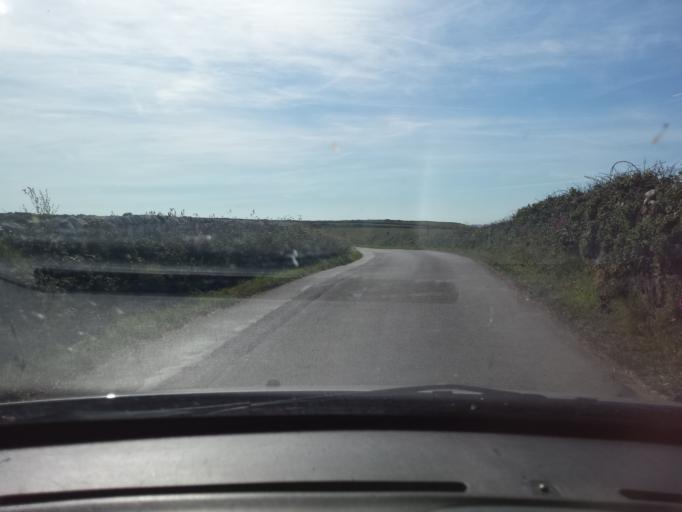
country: FR
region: Lower Normandy
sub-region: Departement de la Manche
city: Beaumont-Hague
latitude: 49.6767
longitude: -1.9344
